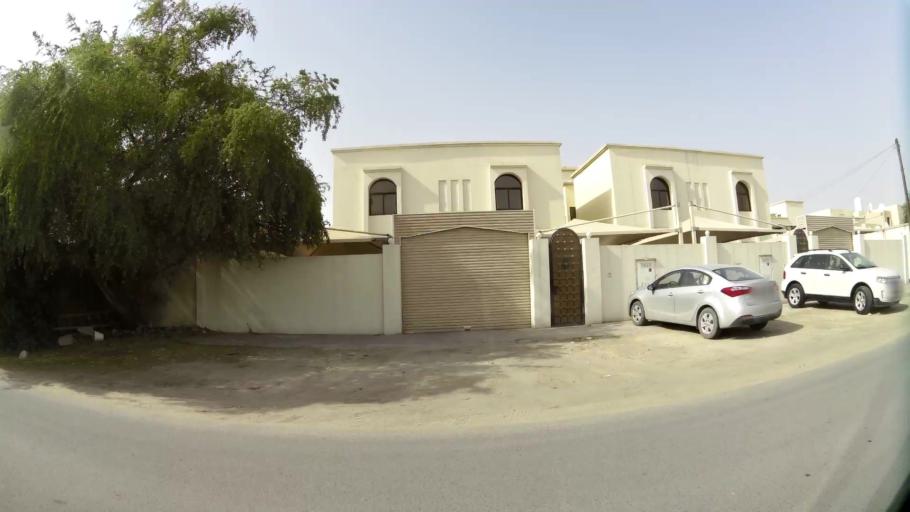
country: QA
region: Baladiyat ar Rayyan
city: Ar Rayyan
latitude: 25.2500
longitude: 51.4407
